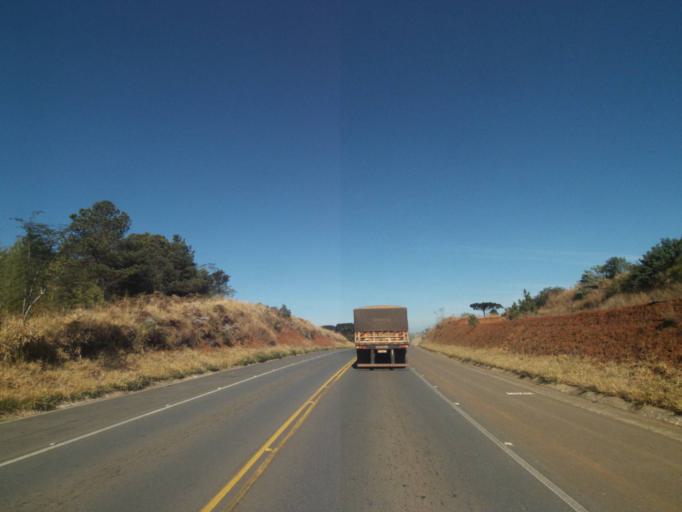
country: BR
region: Parana
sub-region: Tibagi
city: Tibagi
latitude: -24.6015
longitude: -50.4383
